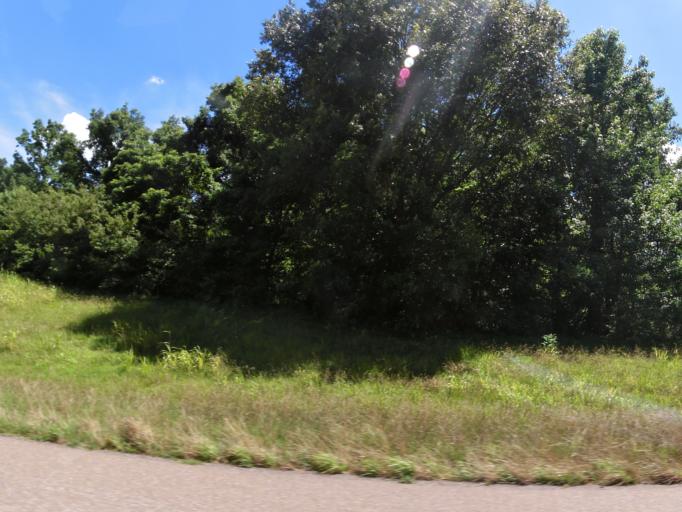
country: US
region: Tennessee
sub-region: Dyer County
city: Dyersburg
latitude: 36.0694
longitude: -89.4428
